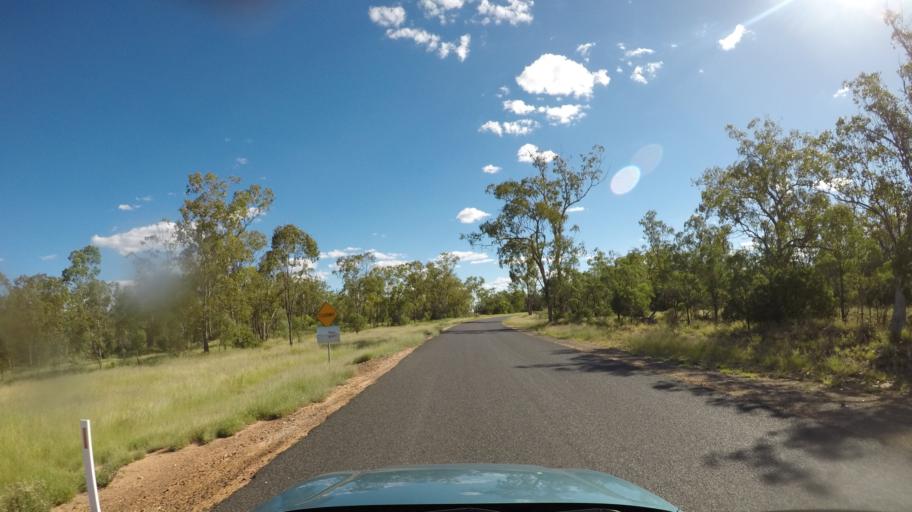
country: AU
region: Queensland
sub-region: Goondiwindi
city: Goondiwindi
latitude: -28.1734
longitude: 150.4712
